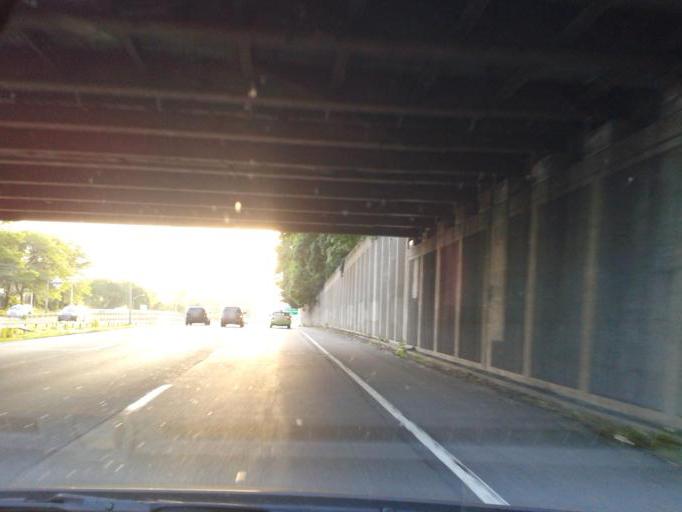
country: US
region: New York
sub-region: Westchester County
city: Bronxville
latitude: 40.9265
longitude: -73.8352
